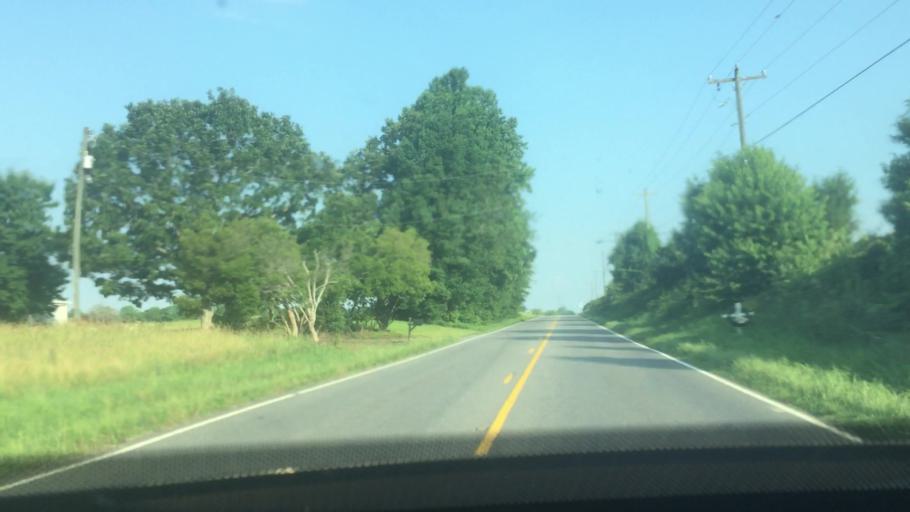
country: US
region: North Carolina
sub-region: Iredell County
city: Mooresville
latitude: 35.5909
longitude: -80.7539
